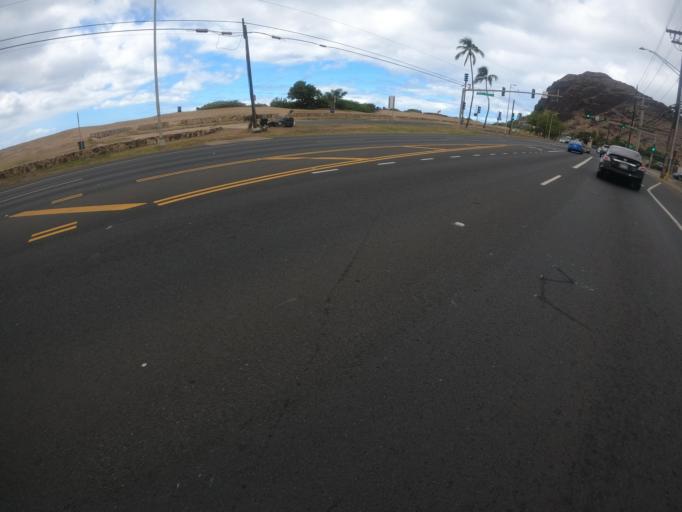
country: US
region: Hawaii
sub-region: Honolulu County
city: Nanakuli
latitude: 21.3942
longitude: -158.1591
